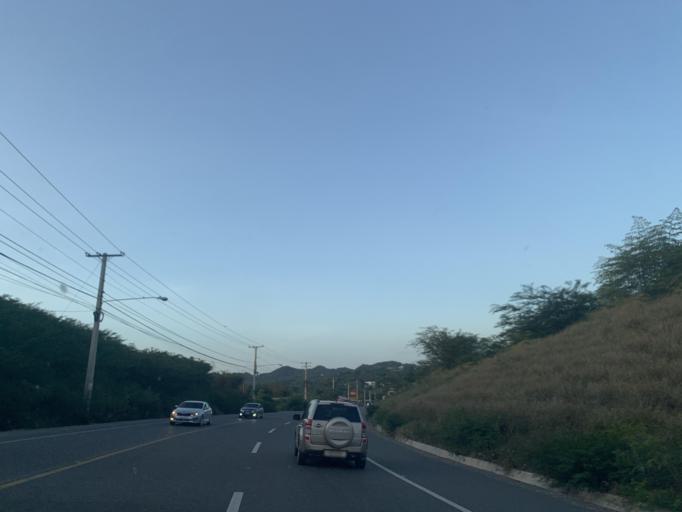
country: DO
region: Puerto Plata
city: Imbert
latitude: 19.7519
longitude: -70.8402
